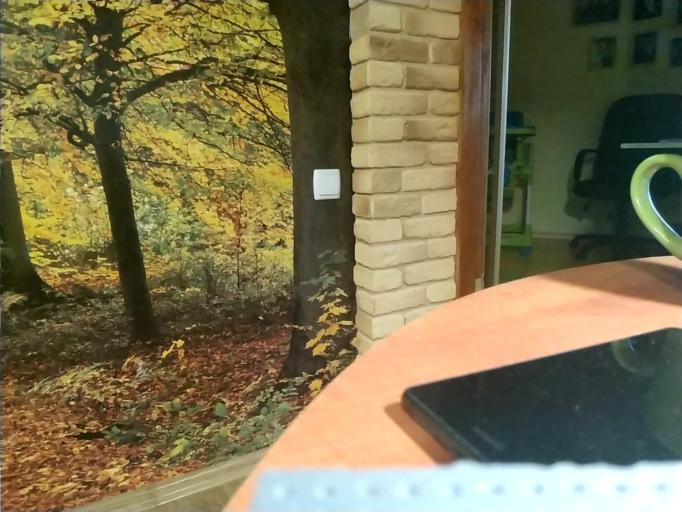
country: RU
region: Moskovskaya
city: Klin
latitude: 56.3553
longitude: 36.7509
